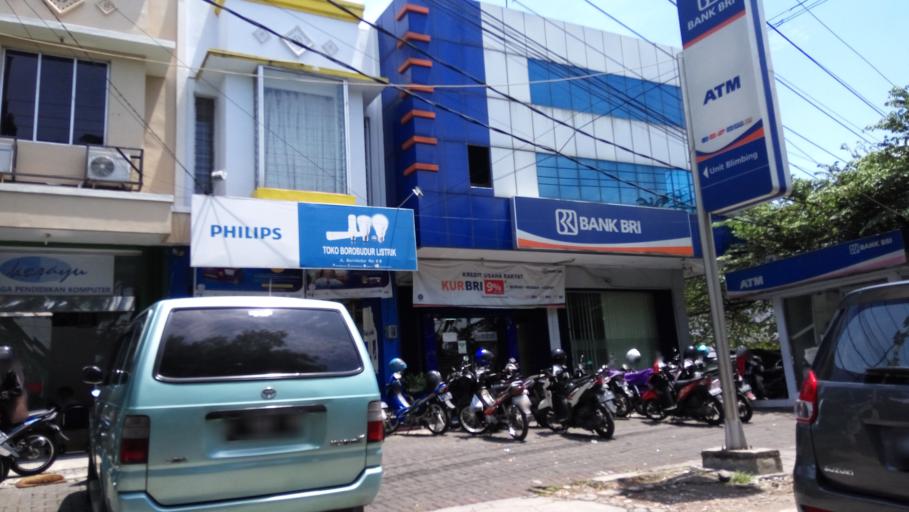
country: ID
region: East Java
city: Malang
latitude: -7.9393
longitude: 112.6368
